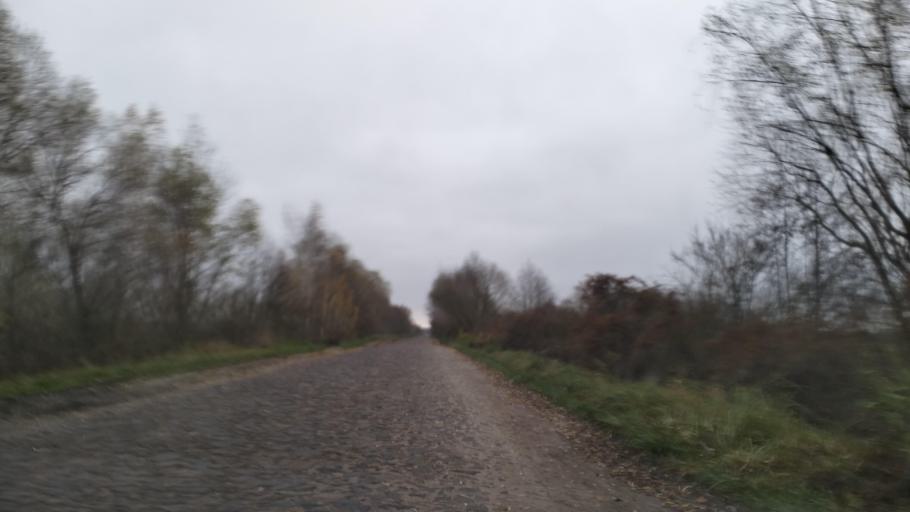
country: BY
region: Brest
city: Davyd-Haradok
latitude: 51.9895
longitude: 27.2054
